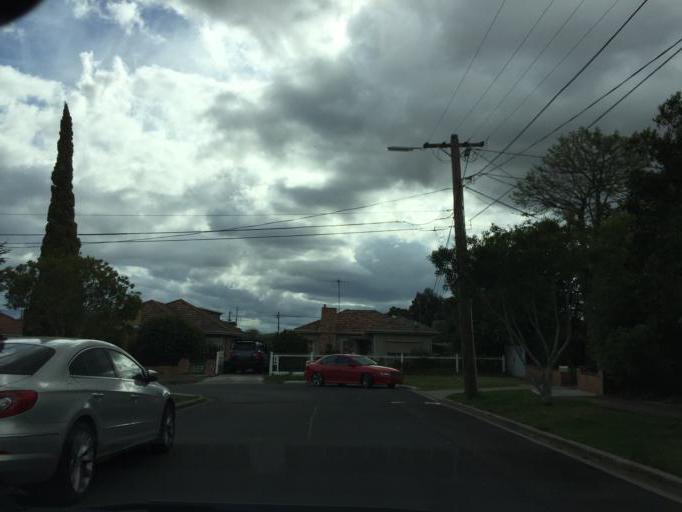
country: AU
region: Victoria
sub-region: Maribyrnong
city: Kingsville
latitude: -37.8065
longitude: 144.8722
